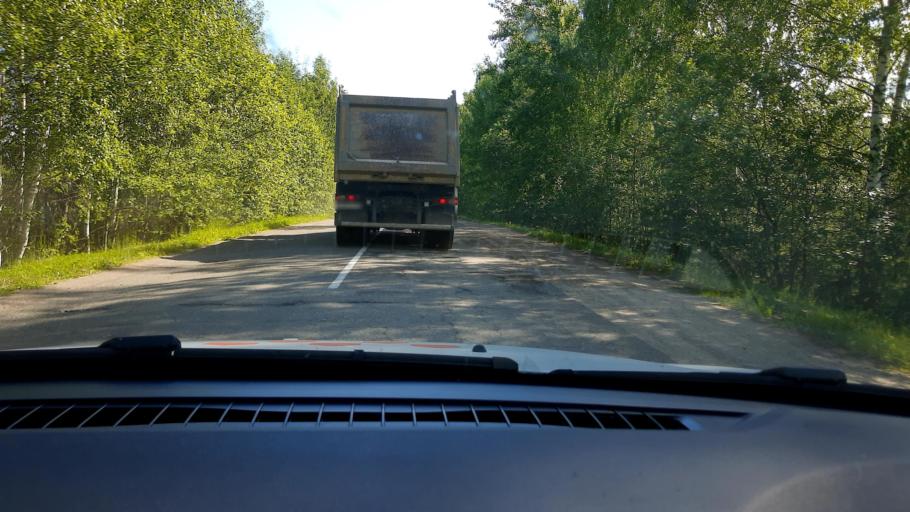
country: RU
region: Nizjnij Novgorod
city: Dal'neye Konstantinovo
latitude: 55.9291
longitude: 43.9897
